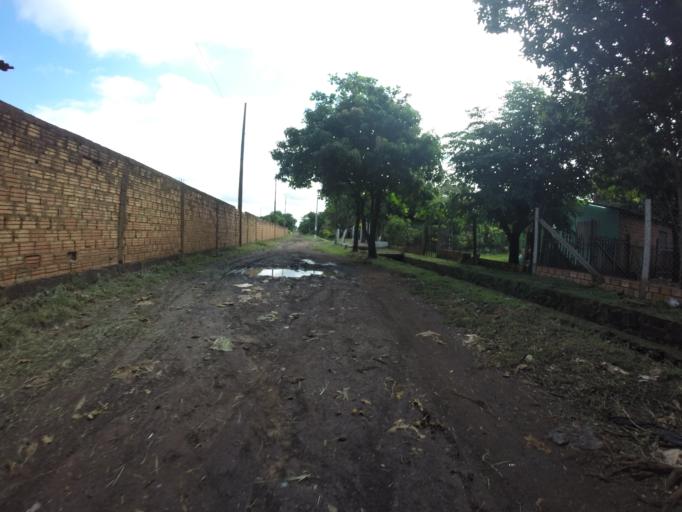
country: PY
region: Alto Parana
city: Ciudad del Este
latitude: -25.3978
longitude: -54.6496
